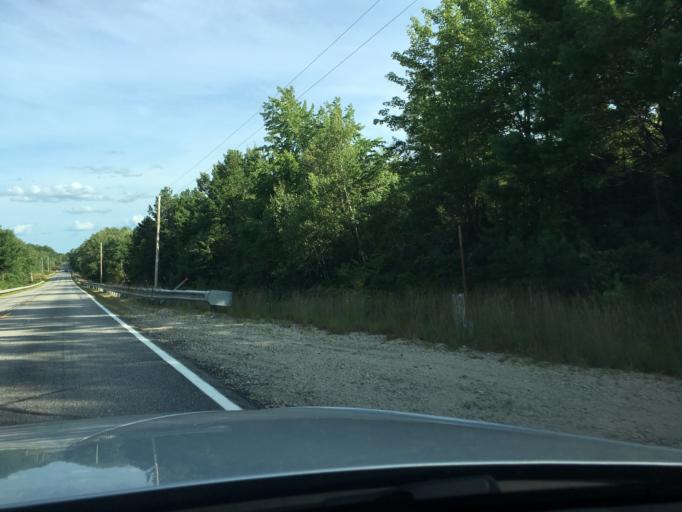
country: US
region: Maine
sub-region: Oxford County
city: Brownfield
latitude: 43.9199
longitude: -70.8596
